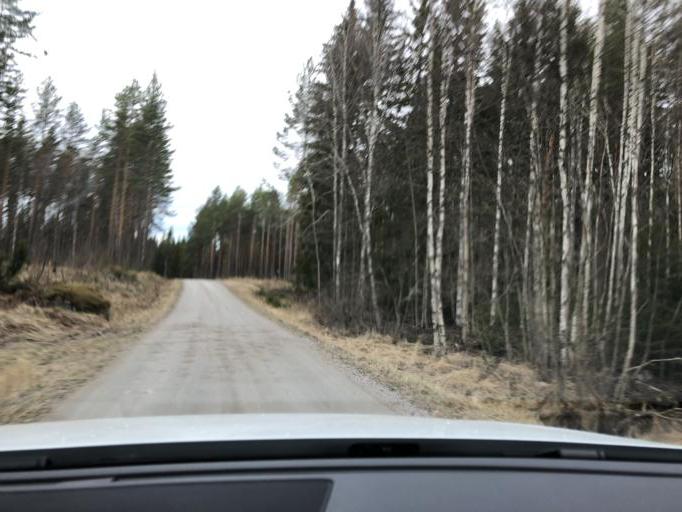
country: SE
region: Gaevleborg
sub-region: Gavle Kommun
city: Hedesunda
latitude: 60.3187
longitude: 17.1038
